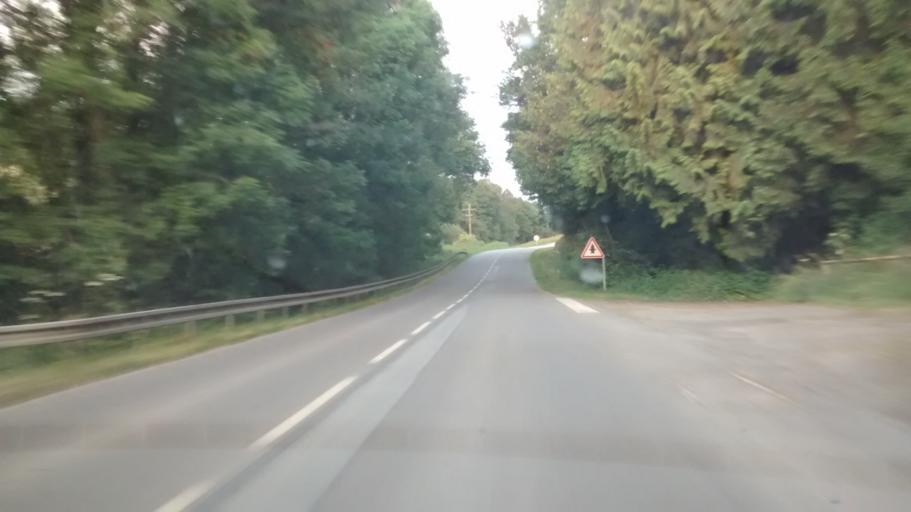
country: FR
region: Brittany
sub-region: Departement du Morbihan
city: Beignon
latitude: 47.9535
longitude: -2.1408
